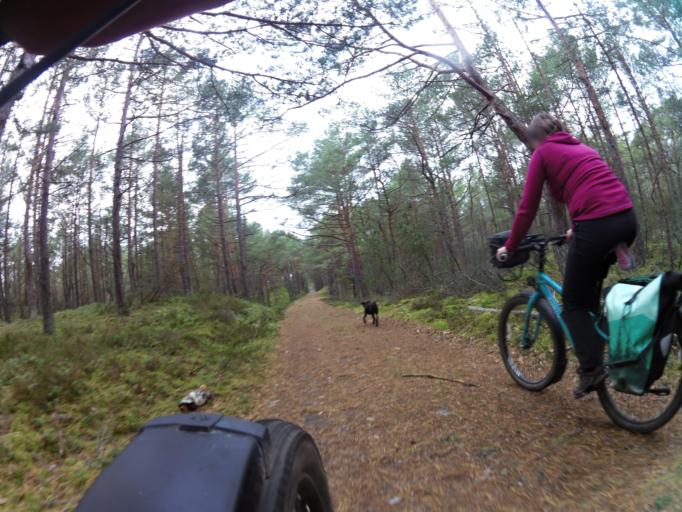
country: PL
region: Pomeranian Voivodeship
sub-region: Powiat pucki
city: Hel
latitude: 54.6297
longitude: 18.8110
